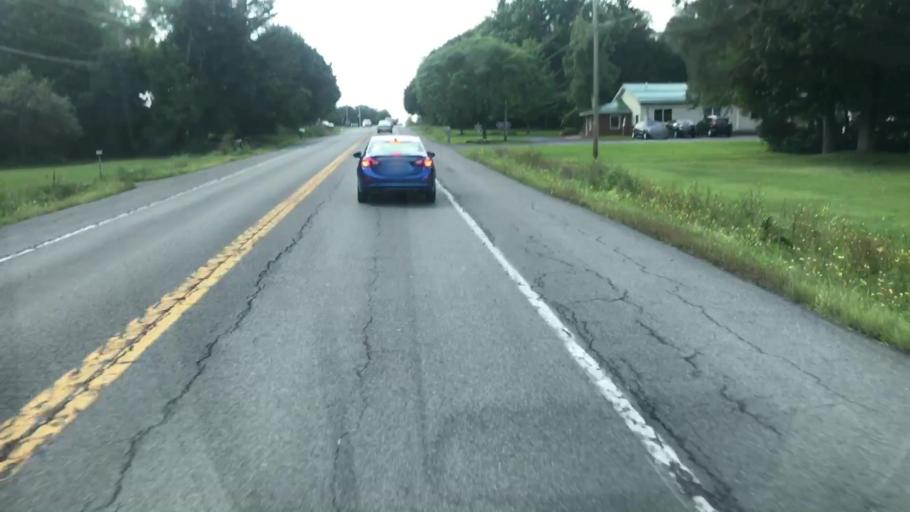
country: US
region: New York
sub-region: Onondaga County
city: Skaneateles
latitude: 42.9435
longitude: -76.4563
